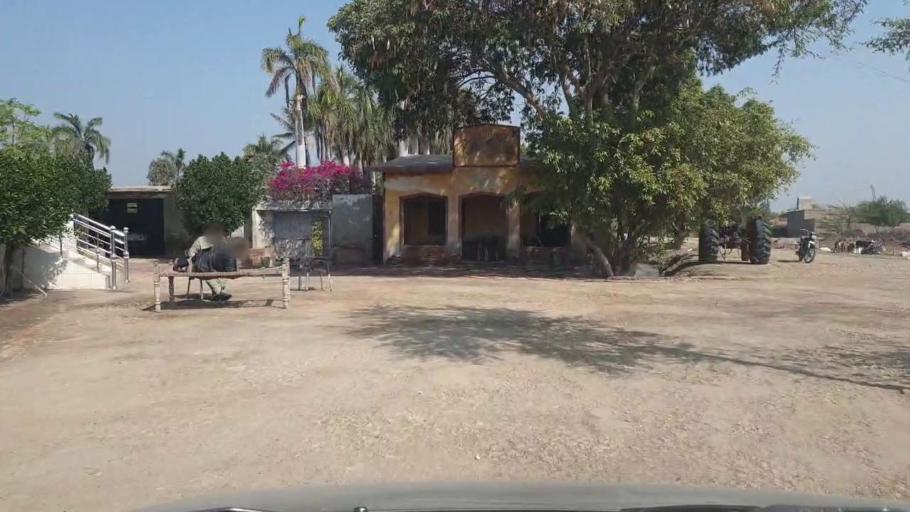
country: PK
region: Sindh
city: Mirwah Gorchani
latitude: 25.2566
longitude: 69.1277
